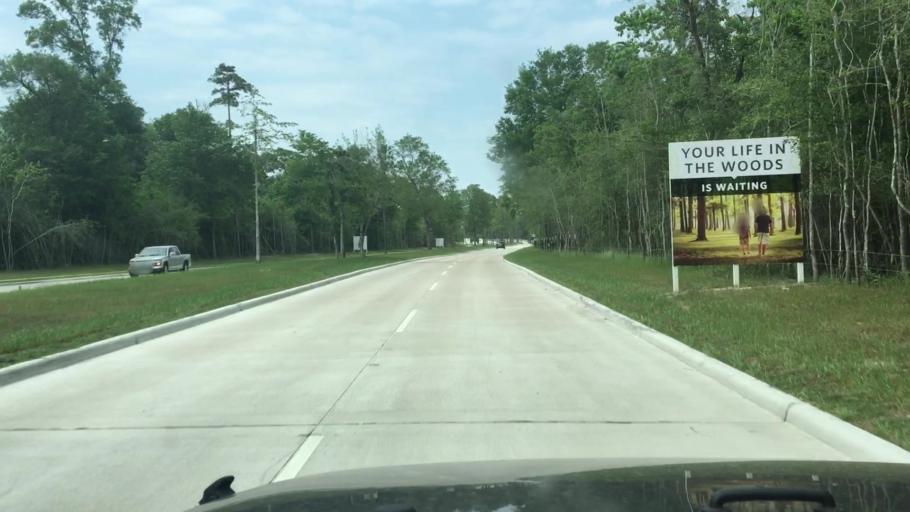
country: US
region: Texas
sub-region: Harris County
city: Atascocita
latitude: 29.9548
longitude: -95.2101
